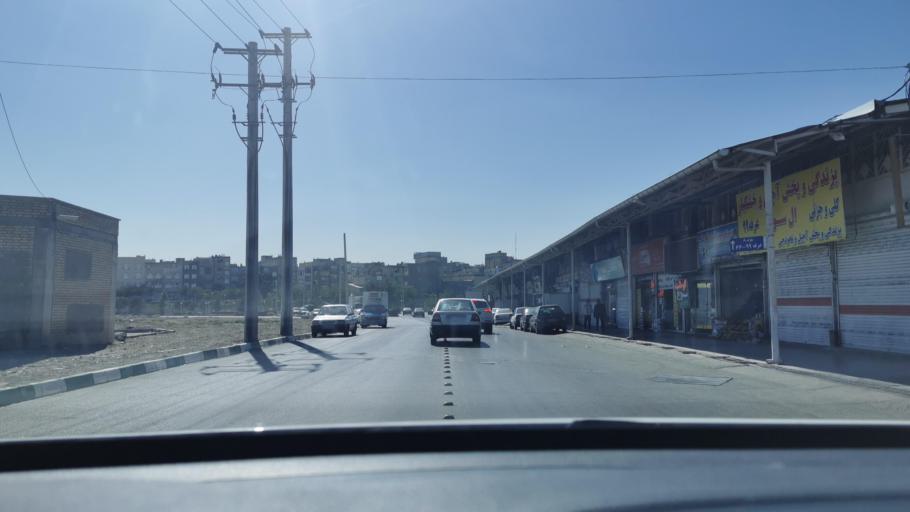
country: IR
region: Razavi Khorasan
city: Mashhad
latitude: 36.3353
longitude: 59.6190
